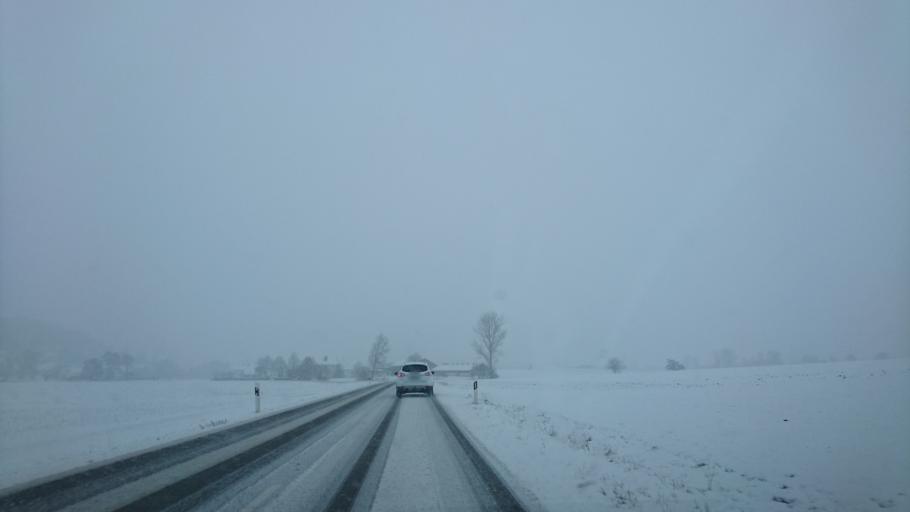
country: DE
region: Bavaria
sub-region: Swabia
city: Laugna
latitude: 48.5166
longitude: 10.6851
